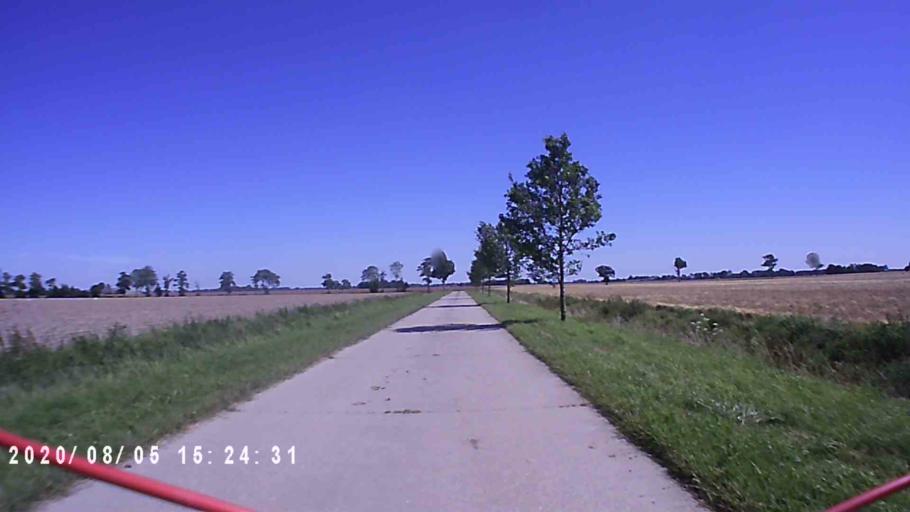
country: NL
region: Groningen
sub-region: Gemeente Winsum
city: Winsum
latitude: 53.3431
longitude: 6.4537
